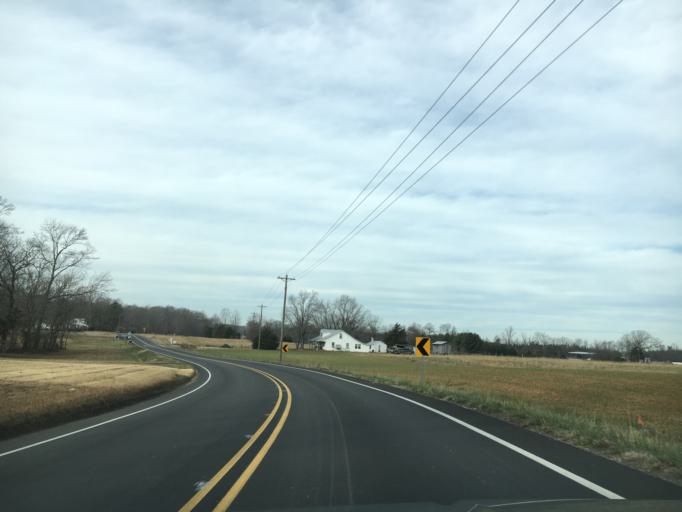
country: US
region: Virginia
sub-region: Goochland County
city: Goochland
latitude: 37.8161
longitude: -77.8725
